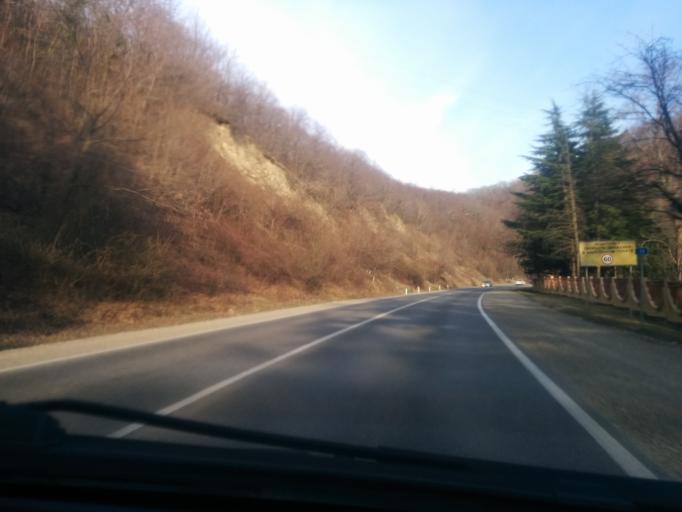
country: RU
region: Krasnodarskiy
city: Novomikhaylovskiy
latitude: 44.2591
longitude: 38.8267
